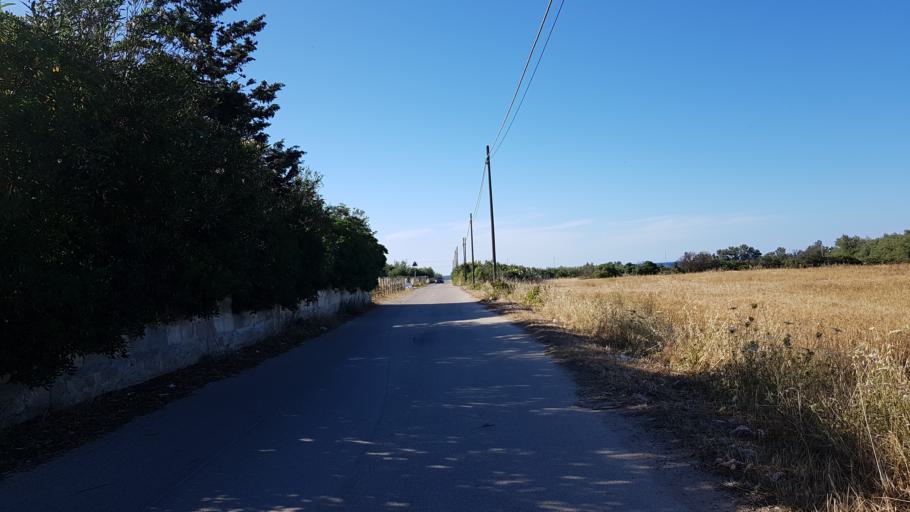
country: IT
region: Apulia
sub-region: Provincia di Brindisi
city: Brindisi
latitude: 40.6820
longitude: 17.8755
